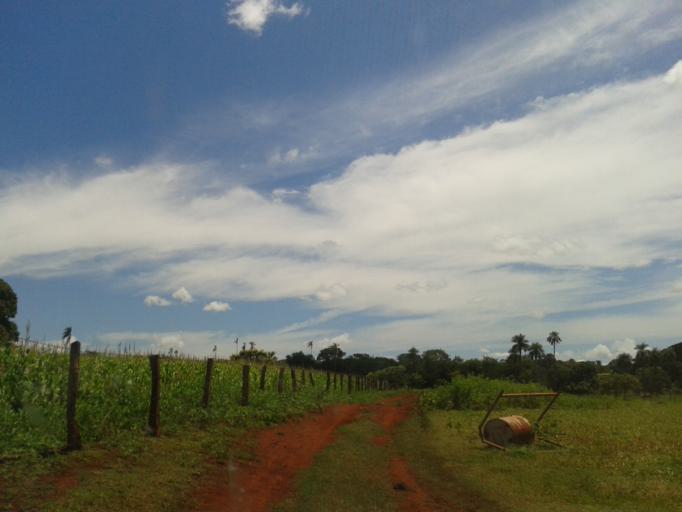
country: BR
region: Minas Gerais
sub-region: Capinopolis
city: Capinopolis
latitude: -18.7757
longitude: -49.8133
